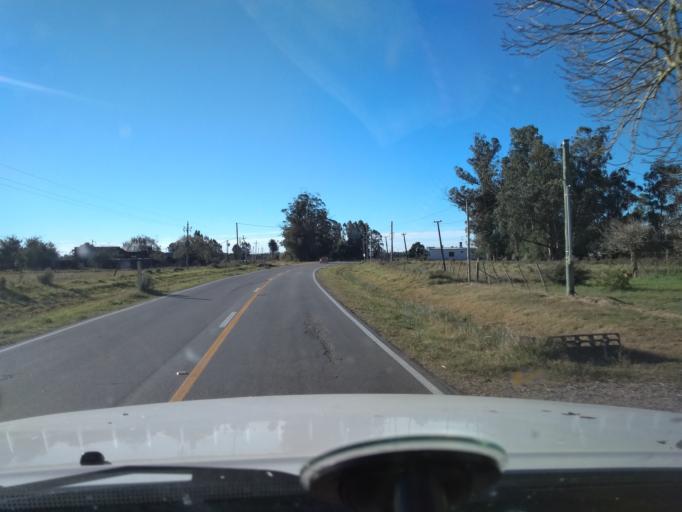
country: UY
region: Canelones
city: Santa Rosa
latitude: -34.5119
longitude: -56.0540
